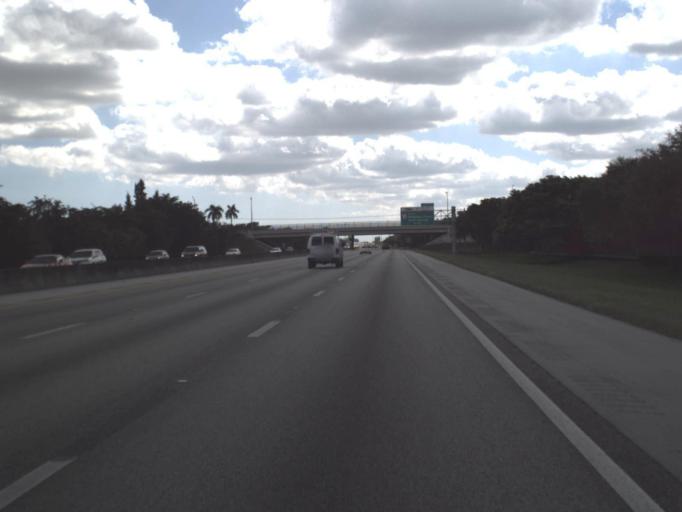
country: US
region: Florida
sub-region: Palm Beach County
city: Boca Pointe
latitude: 26.3208
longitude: -80.1703
